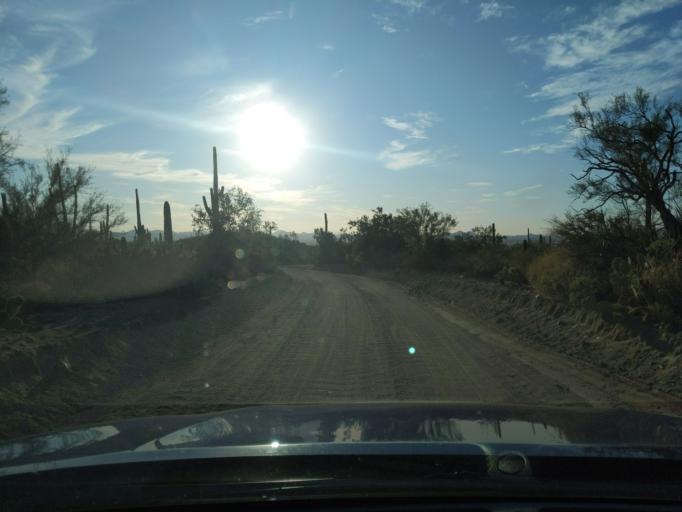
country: US
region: Arizona
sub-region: Pima County
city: Picture Rocks
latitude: 32.2879
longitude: -111.1928
